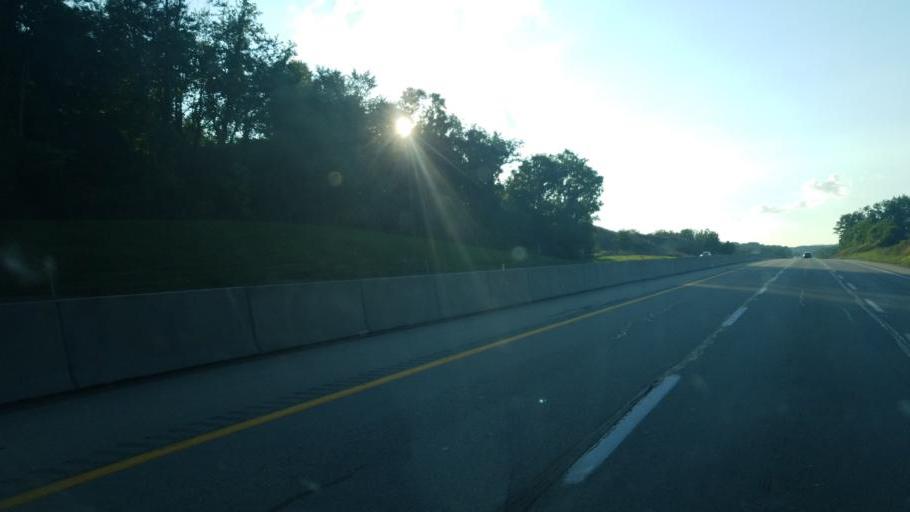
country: US
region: Pennsylvania
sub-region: Lawrence County
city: New Beaver
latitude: 40.8724
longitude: -80.4096
